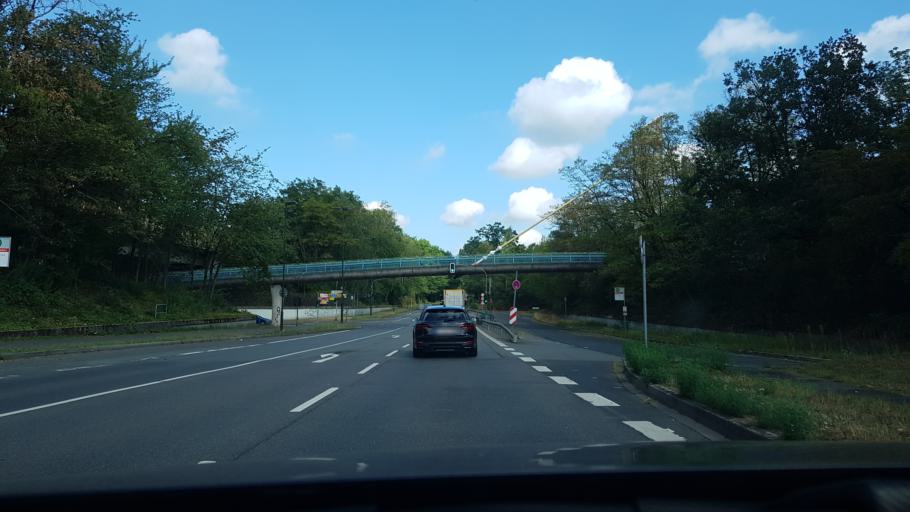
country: DE
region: North Rhine-Westphalia
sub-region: Regierungsbezirk Dusseldorf
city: Hilden
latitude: 51.1326
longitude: 6.9105
